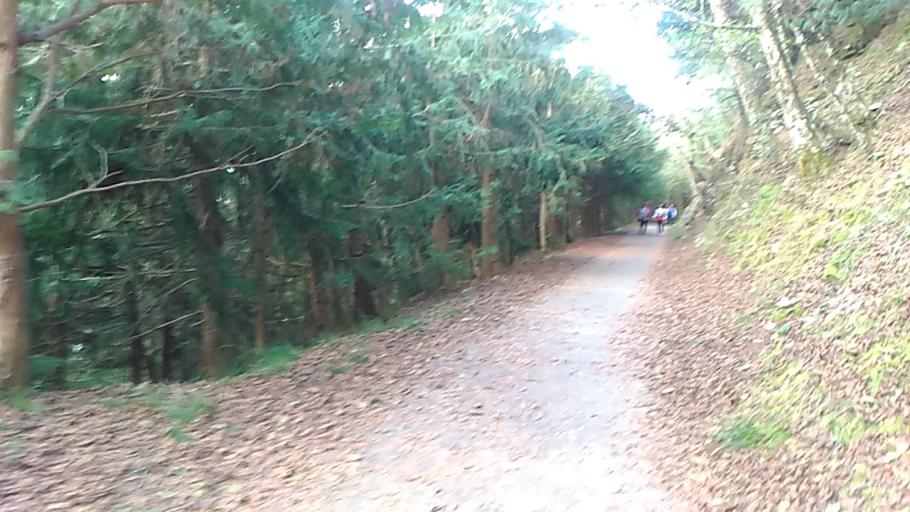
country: TW
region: Taiwan
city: Daxi
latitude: 24.4094
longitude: 121.3031
